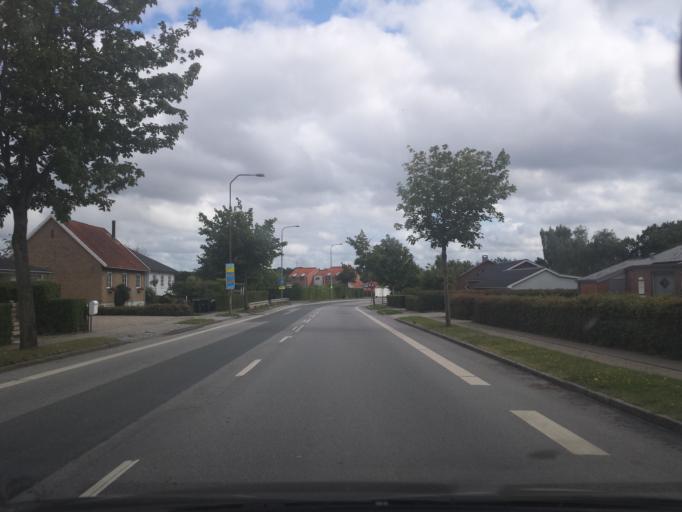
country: DK
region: South Denmark
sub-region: Sonderborg Kommune
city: Grasten
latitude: 54.9251
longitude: 9.6026
